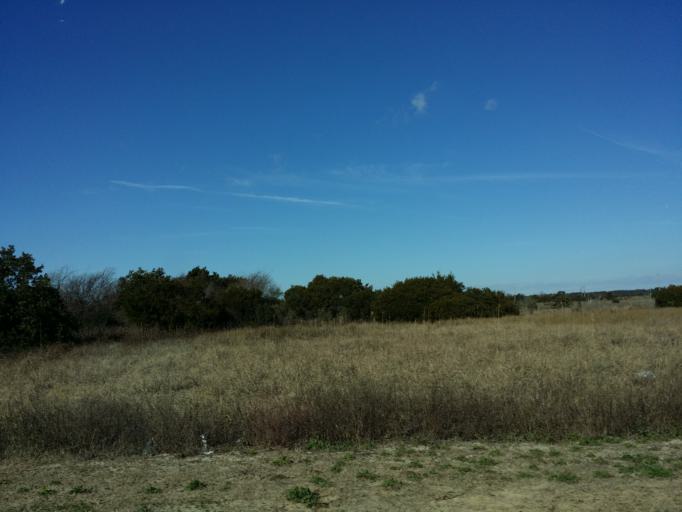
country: US
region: North Carolina
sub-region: Onslow County
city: Sneads Ferry
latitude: 34.4776
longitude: -77.4529
